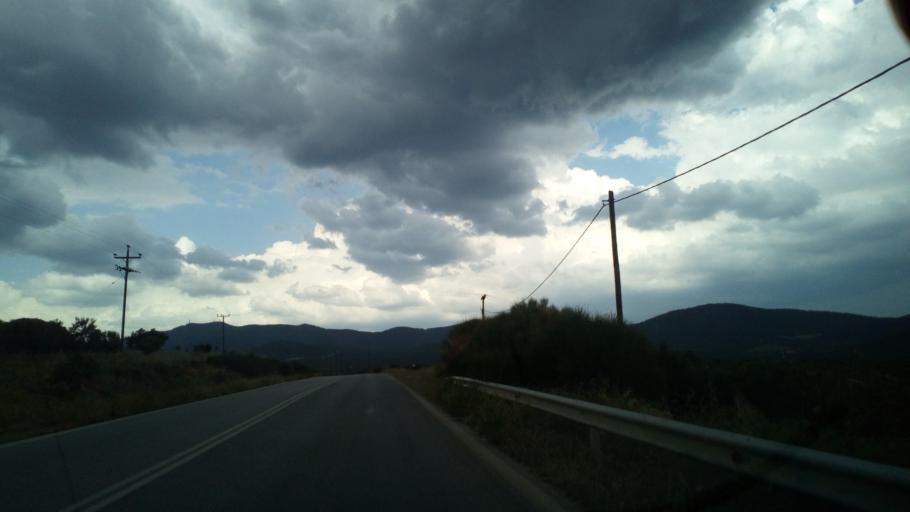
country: GR
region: Central Macedonia
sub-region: Nomos Chalkidikis
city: Polygyros
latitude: 40.3243
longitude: 23.4490
